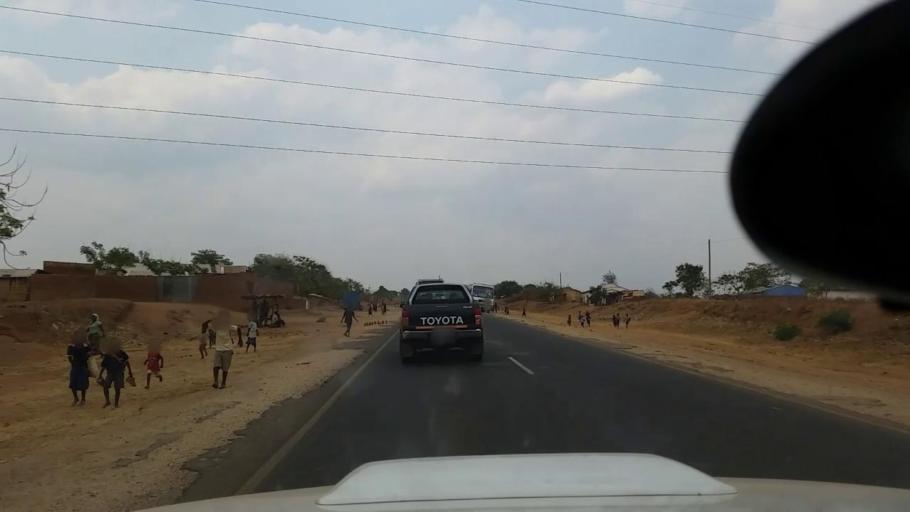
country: MW
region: Central Region
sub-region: Lilongwe District
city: Lilongwe
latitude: -13.8651
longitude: 33.8297
